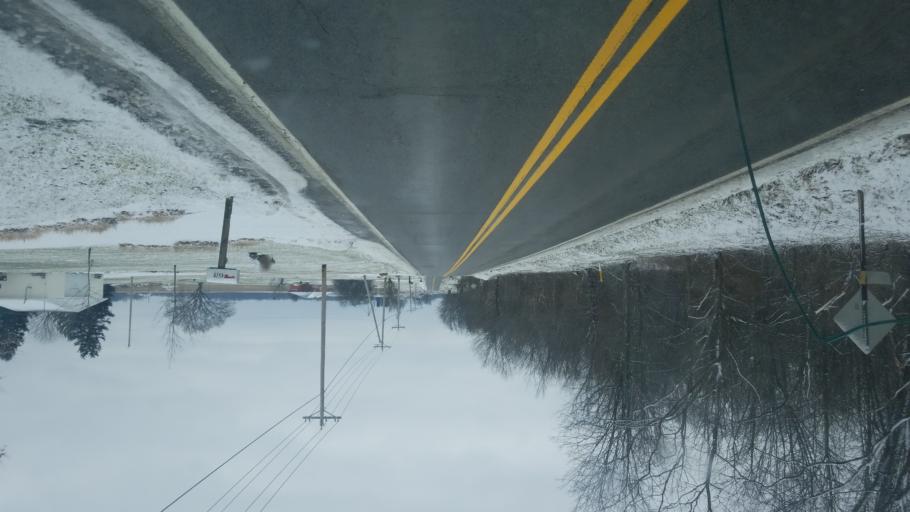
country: US
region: Ohio
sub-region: Licking County
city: Johnstown
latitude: 40.1217
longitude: -82.6974
